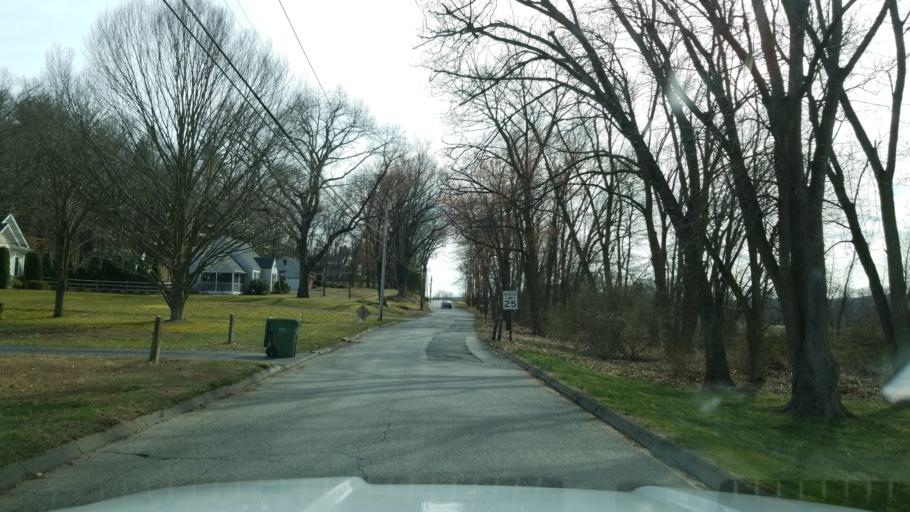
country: US
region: Connecticut
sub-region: Hartford County
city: Glastonbury Center
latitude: 41.6604
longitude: -72.6183
